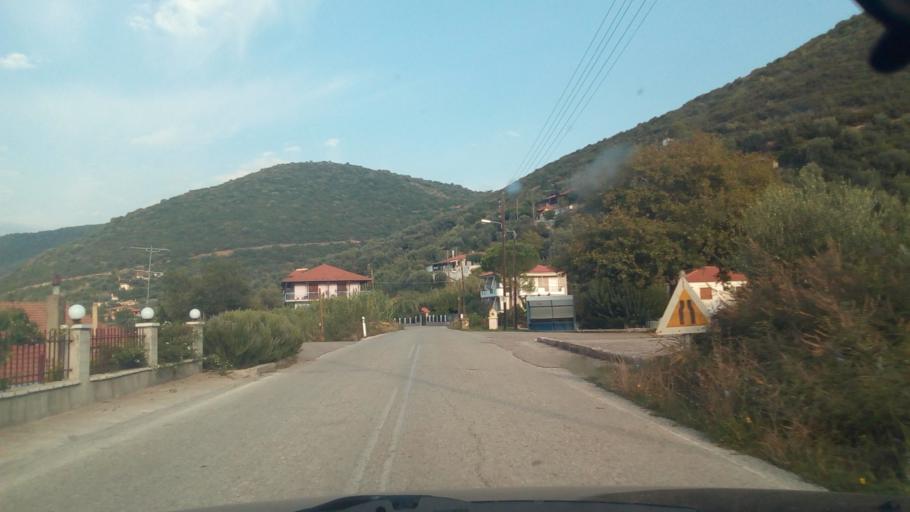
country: GR
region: West Greece
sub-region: Nomos Aitolias kai Akarnanias
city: Nafpaktos
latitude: 38.4251
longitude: 21.9131
